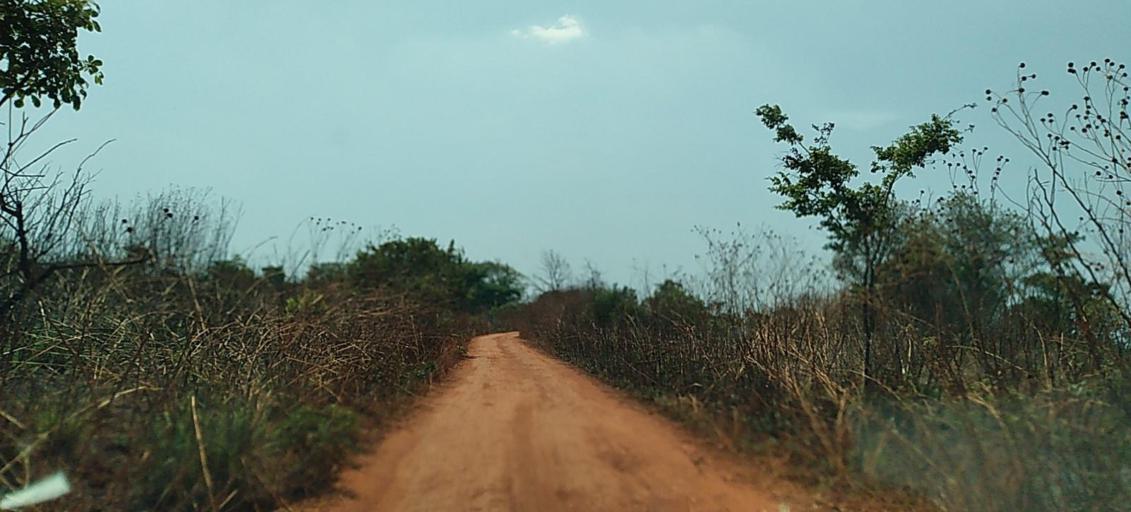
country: ZM
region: North-Western
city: Solwezi
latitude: -12.1338
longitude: 26.3173
